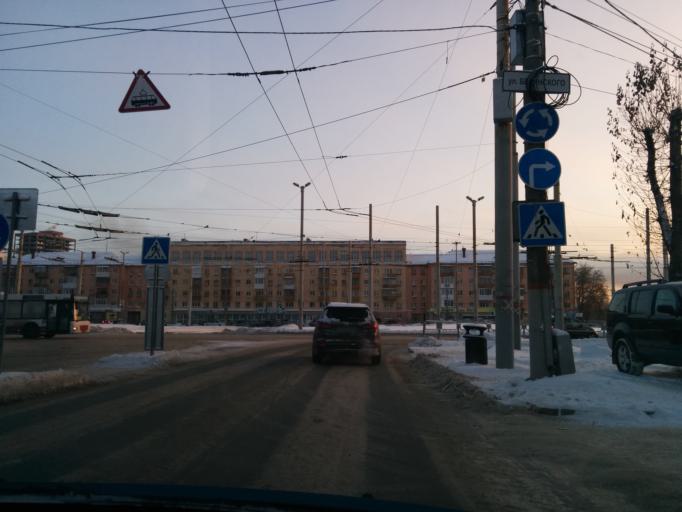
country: RU
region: Perm
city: Perm
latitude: 57.9976
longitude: 56.2614
